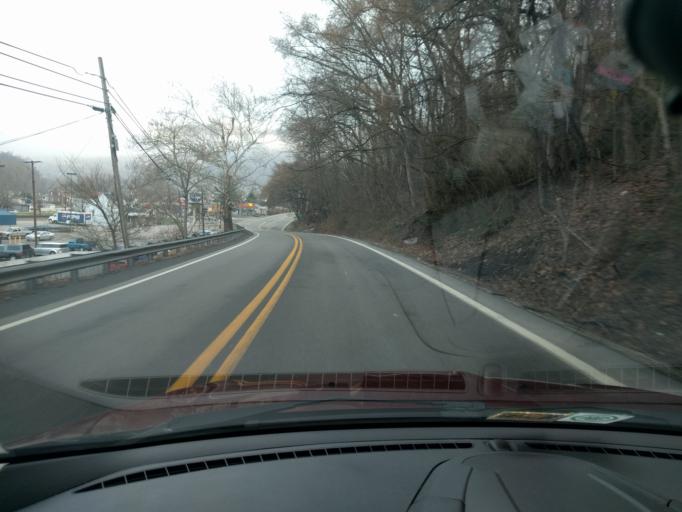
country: US
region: West Virginia
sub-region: Kanawha County
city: Montgomery
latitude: 38.1702
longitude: -81.3030
